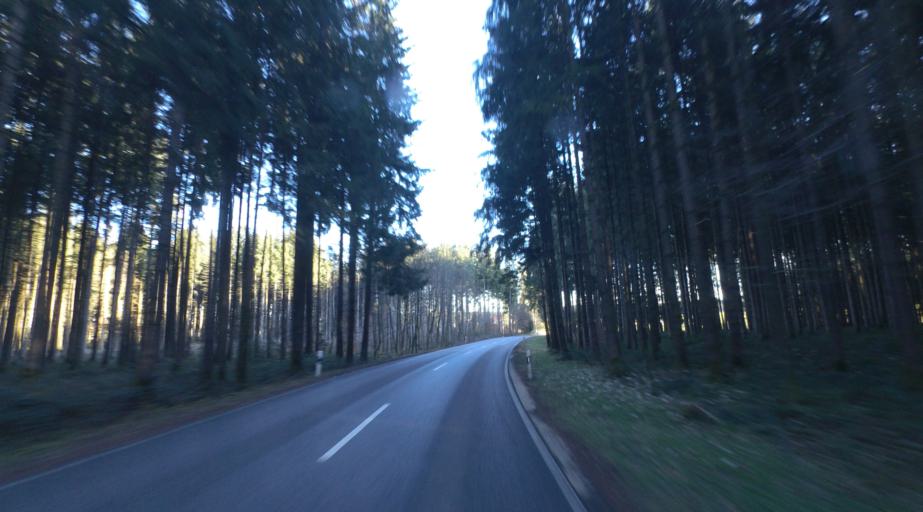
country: DE
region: Bavaria
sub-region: Upper Bavaria
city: Trostberg an der Alz
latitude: 48.0218
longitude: 12.5806
